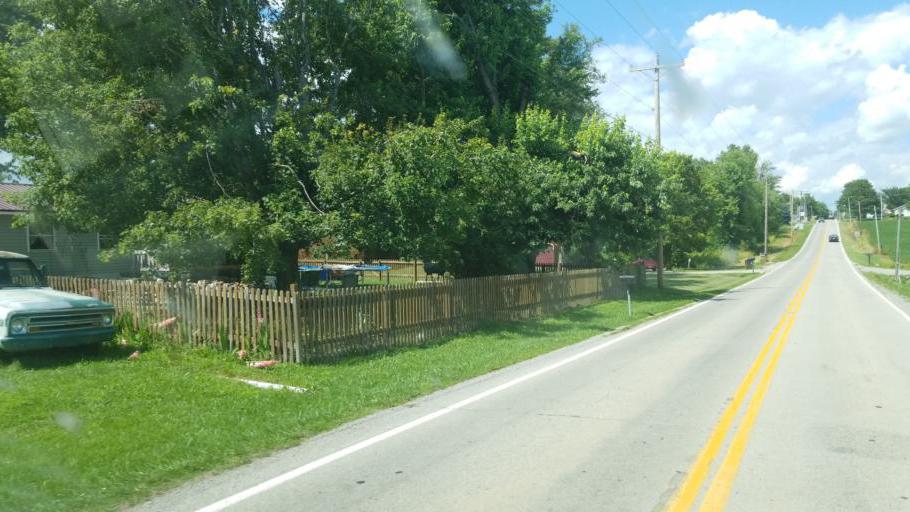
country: US
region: Ohio
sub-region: Highland County
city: Greenfield
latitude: 39.3379
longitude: -83.3950
